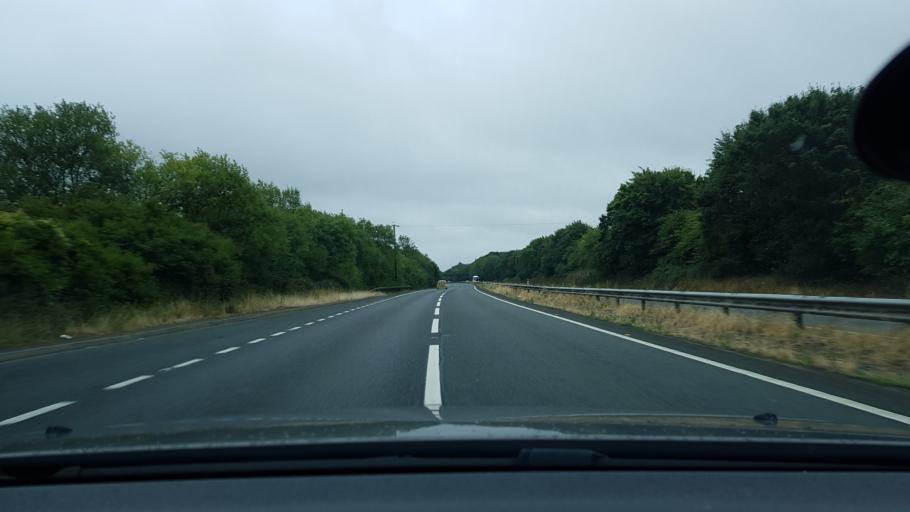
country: GB
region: England
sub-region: Hampshire
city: Highclere
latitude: 51.3215
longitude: -1.3406
